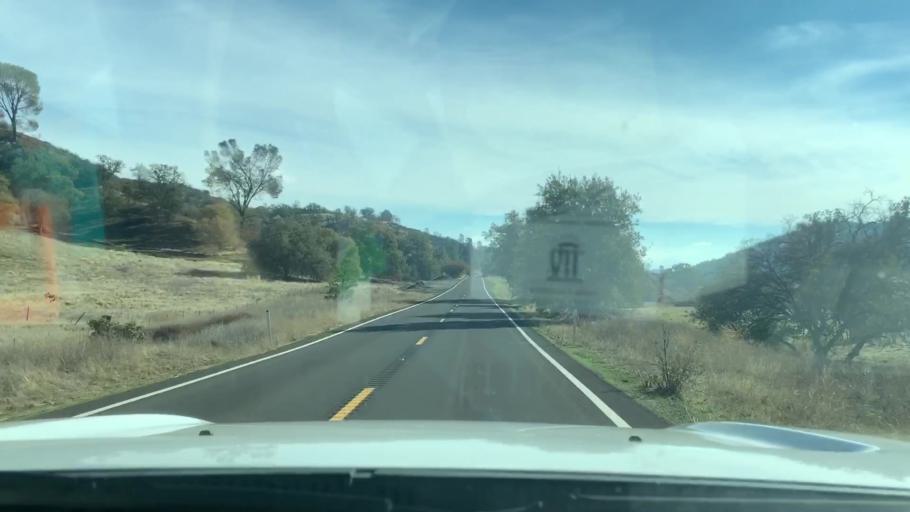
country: US
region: California
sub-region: Fresno County
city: Coalinga
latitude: 36.1166
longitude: -120.5779
